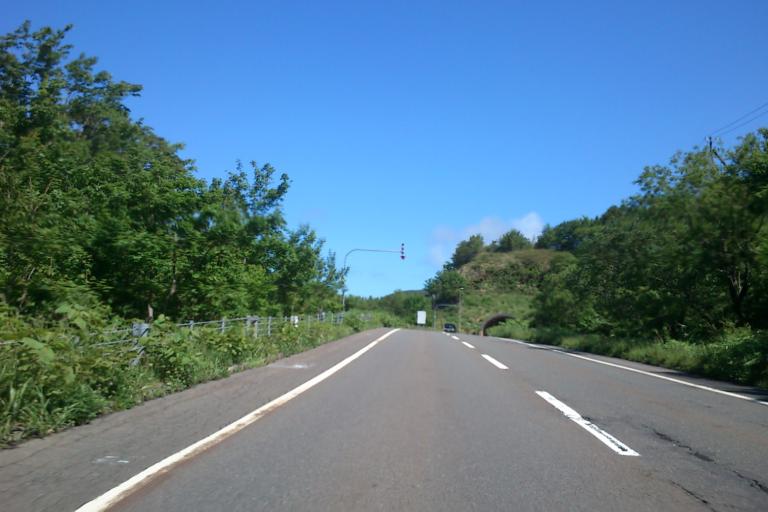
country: JP
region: Hokkaido
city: Ishikari
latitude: 43.4968
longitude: 141.3739
